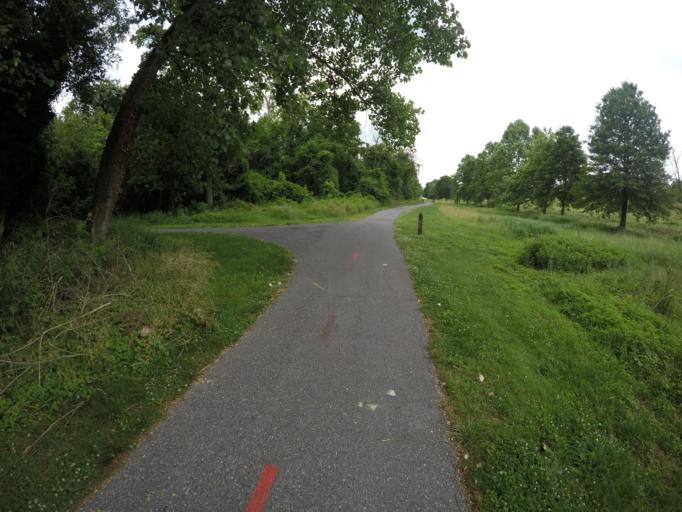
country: US
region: Maryland
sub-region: Prince George's County
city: Brentwood
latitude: 38.9484
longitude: -76.9524
